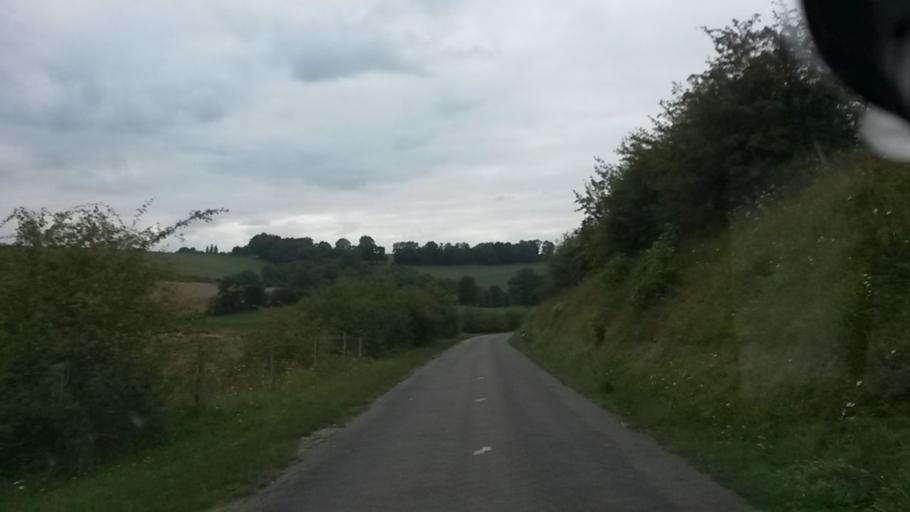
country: FR
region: Haute-Normandie
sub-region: Departement de la Seine-Maritime
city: La Feuillie
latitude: 49.4817
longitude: 1.5215
